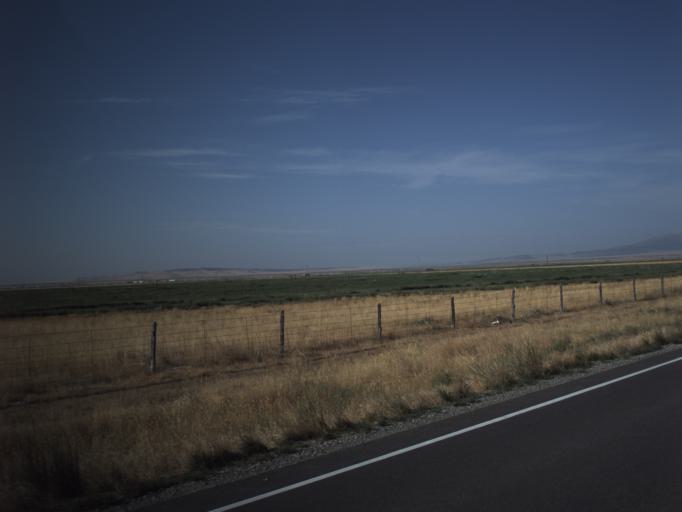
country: US
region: Idaho
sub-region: Oneida County
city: Malad City
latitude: 41.9670
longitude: -112.8756
